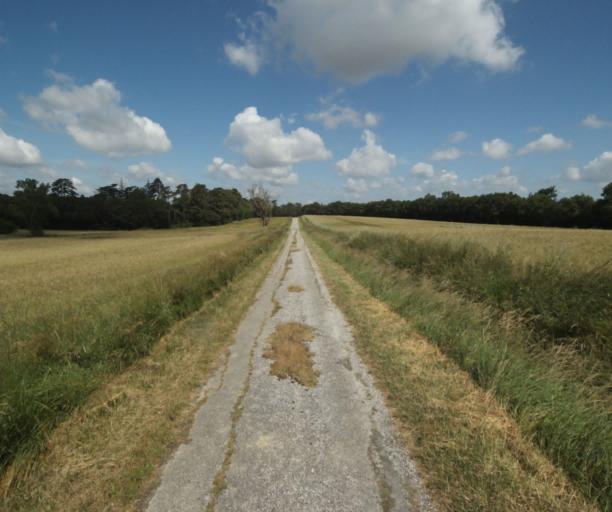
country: FR
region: Midi-Pyrenees
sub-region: Departement de la Haute-Garonne
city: Saint-Felix-Lauragais
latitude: 43.4279
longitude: 1.9299
